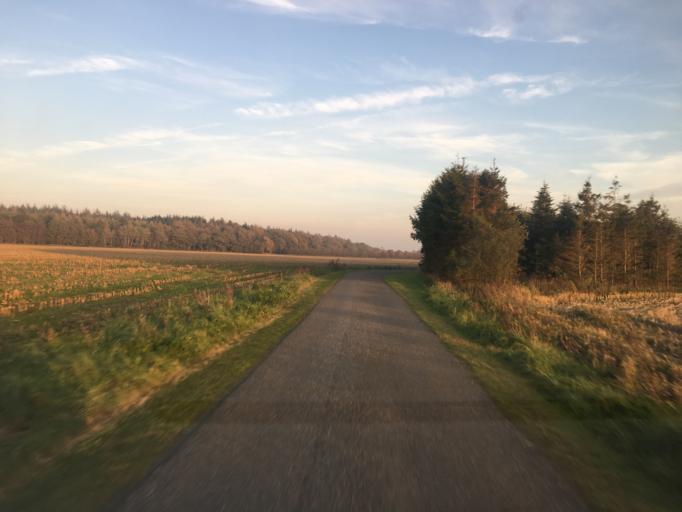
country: DK
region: South Denmark
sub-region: Tonder Kommune
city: Toftlund
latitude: 55.0324
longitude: 9.1195
